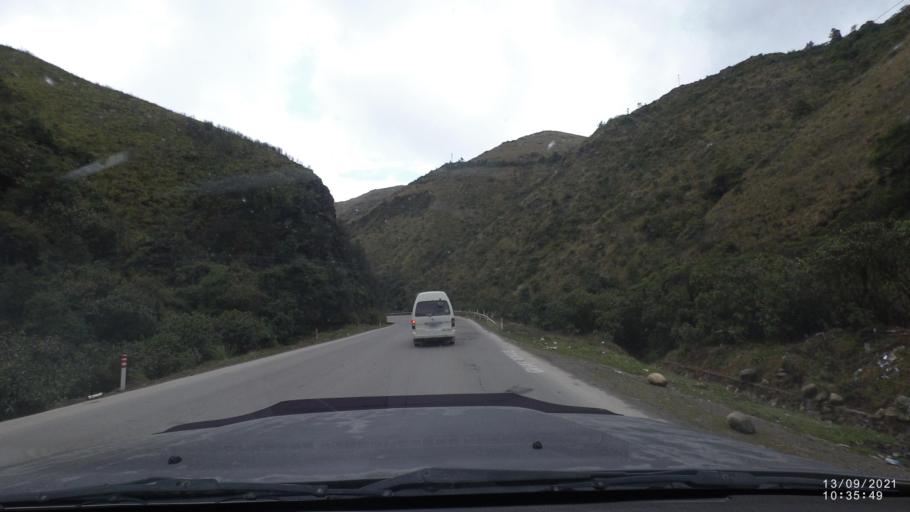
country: BO
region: Cochabamba
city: Colomi
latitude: -17.2151
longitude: -65.8909
